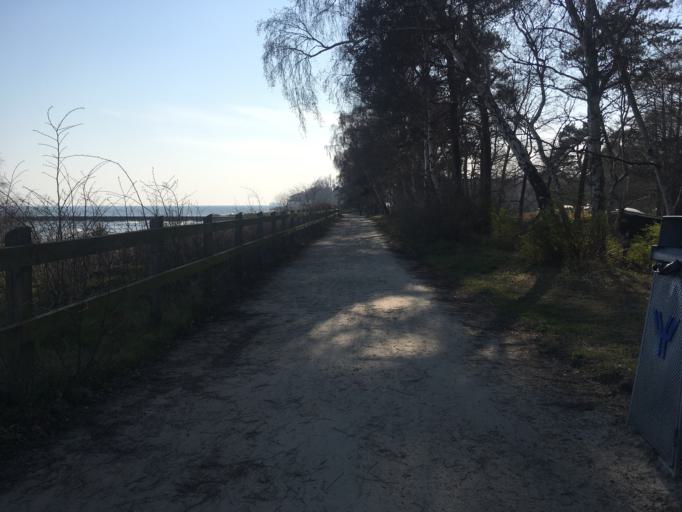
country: SE
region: Skane
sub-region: Ystads Kommun
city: Ystad
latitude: 55.4267
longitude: 13.8526
